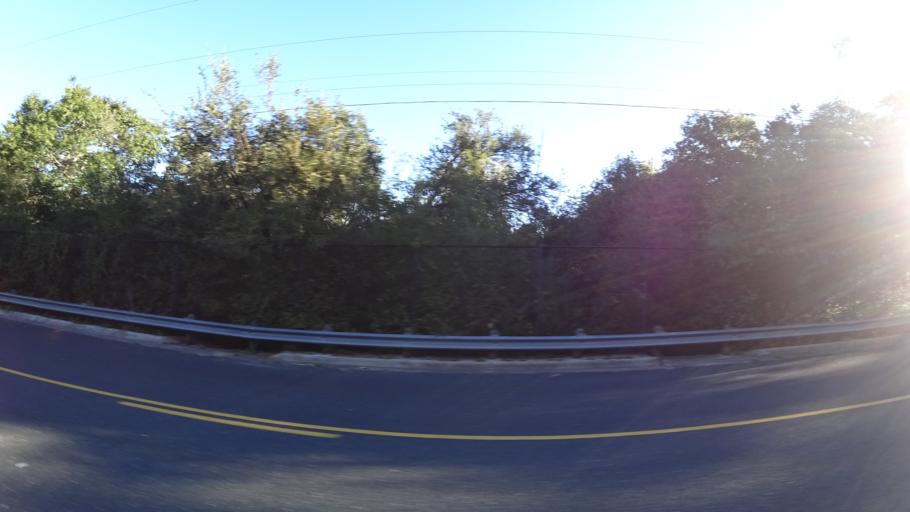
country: US
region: Texas
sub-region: Travis County
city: West Lake Hills
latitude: 30.3414
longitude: -97.8076
